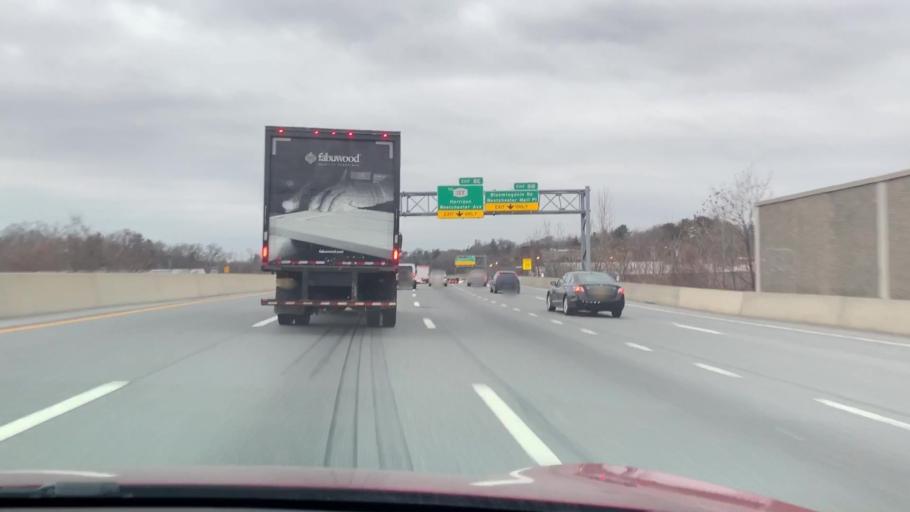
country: US
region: New York
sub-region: Westchester County
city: White Plains
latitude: 41.0364
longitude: -73.7554
